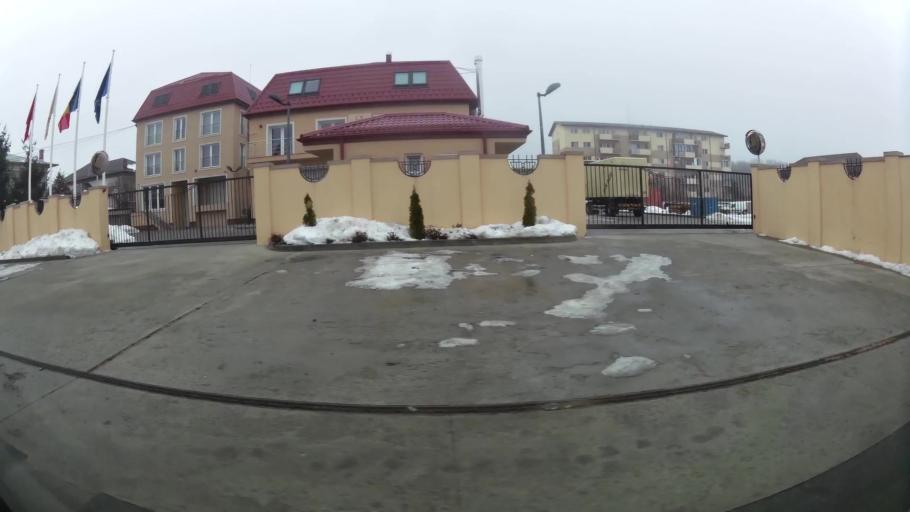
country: RO
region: Ilfov
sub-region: Comuna Chiajna
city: Rosu
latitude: 44.4523
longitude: 26.0028
